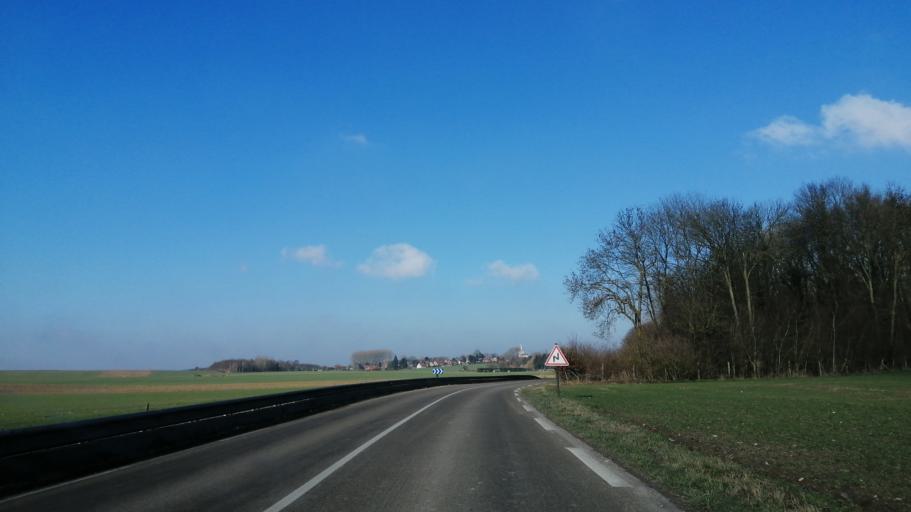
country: FR
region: Nord-Pas-de-Calais
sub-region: Departement du Pas-de-Calais
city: Mont-Saint-Eloi
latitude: 50.3655
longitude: 2.6498
